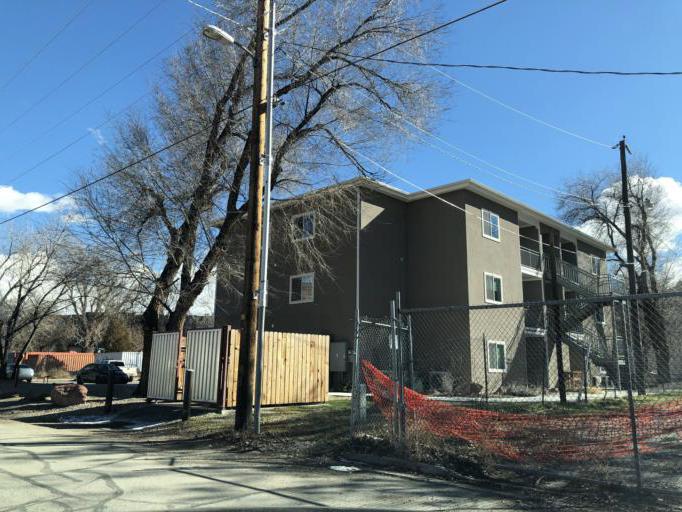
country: US
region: Utah
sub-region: Grand County
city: Moab
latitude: 38.5757
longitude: -109.5555
